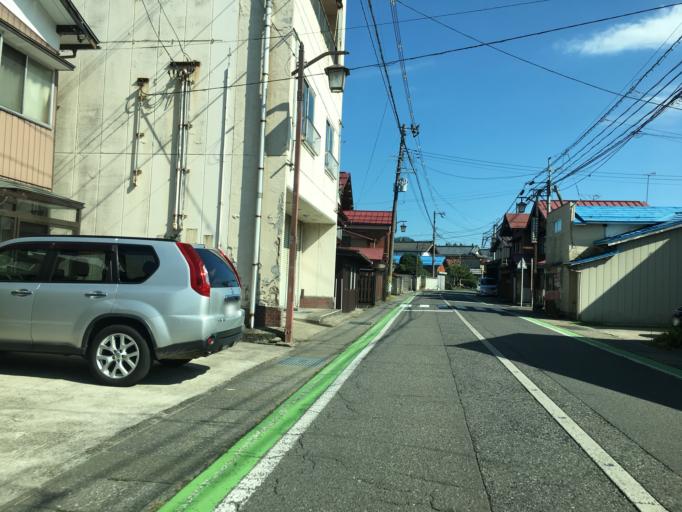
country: JP
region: Niigata
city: Suibara
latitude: 37.6774
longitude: 139.4615
